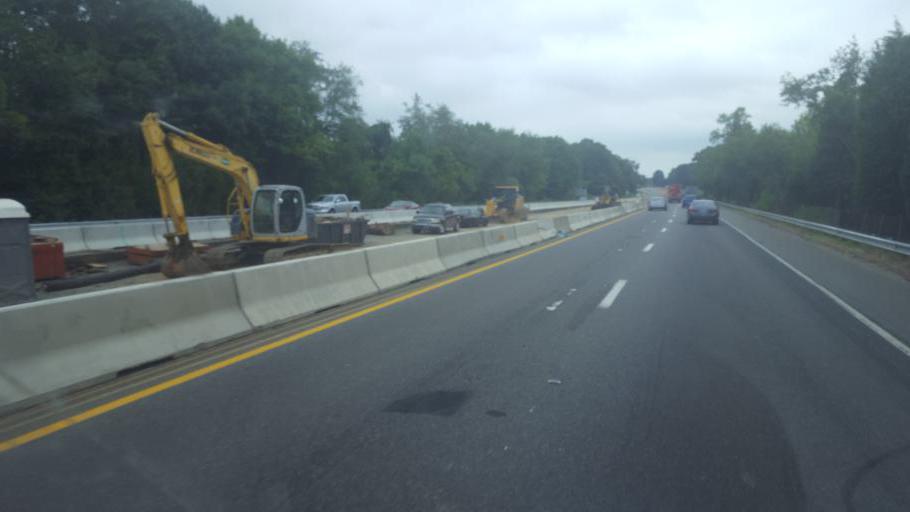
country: US
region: North Carolina
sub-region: Iredell County
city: Mooresville
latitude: 35.5679
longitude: -80.8574
